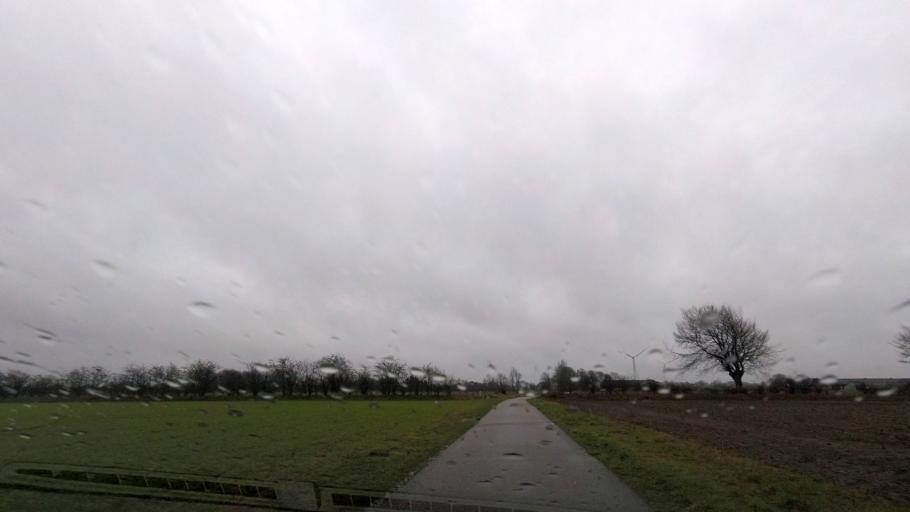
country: DE
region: Schleswig-Holstein
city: Wanderup
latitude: 54.6793
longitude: 9.3058
